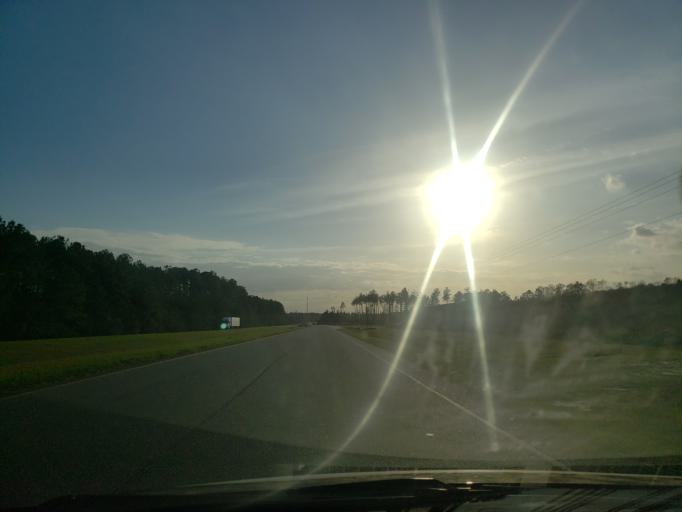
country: US
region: Georgia
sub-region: Chatham County
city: Bloomingdale
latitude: 32.1578
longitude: -81.2725
